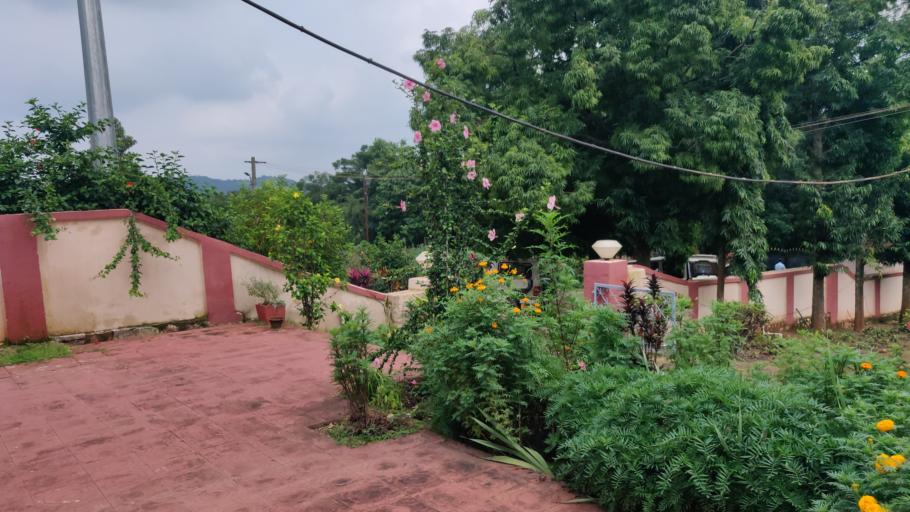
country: IN
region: Odisha
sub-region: Kendujhar
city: Barbil
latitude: 21.6090
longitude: 85.5089
